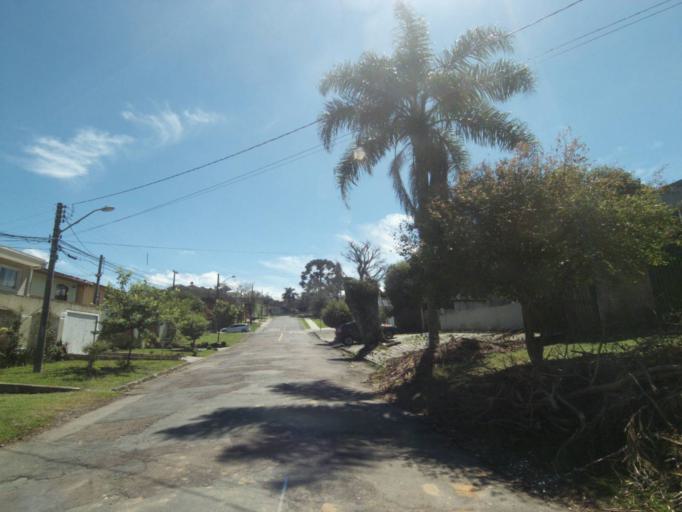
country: BR
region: Parana
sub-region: Curitiba
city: Curitiba
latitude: -25.3897
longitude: -49.2637
